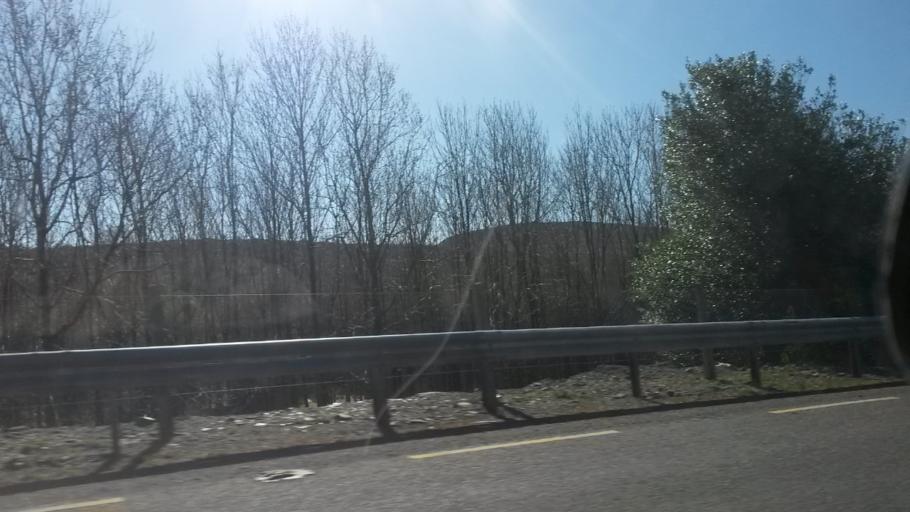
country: IE
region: Munster
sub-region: Ciarrai
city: Cill Airne
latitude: 51.9682
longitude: -9.3504
